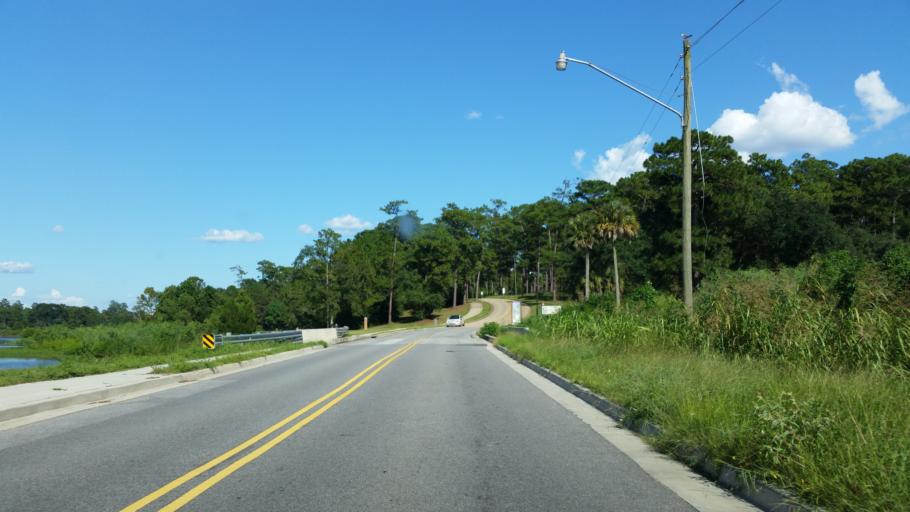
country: US
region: Alabama
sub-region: Mobile County
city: Prichard
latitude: 30.7038
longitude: -88.1626
